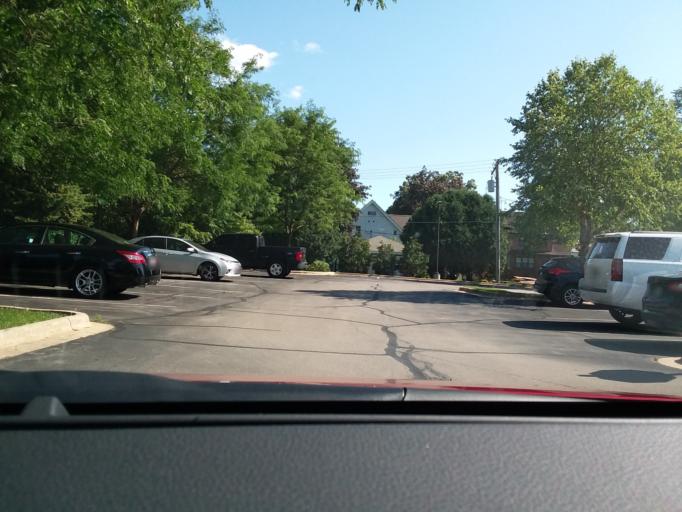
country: US
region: Wisconsin
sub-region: Dane County
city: Waunakee
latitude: 43.1918
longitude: -89.4509
